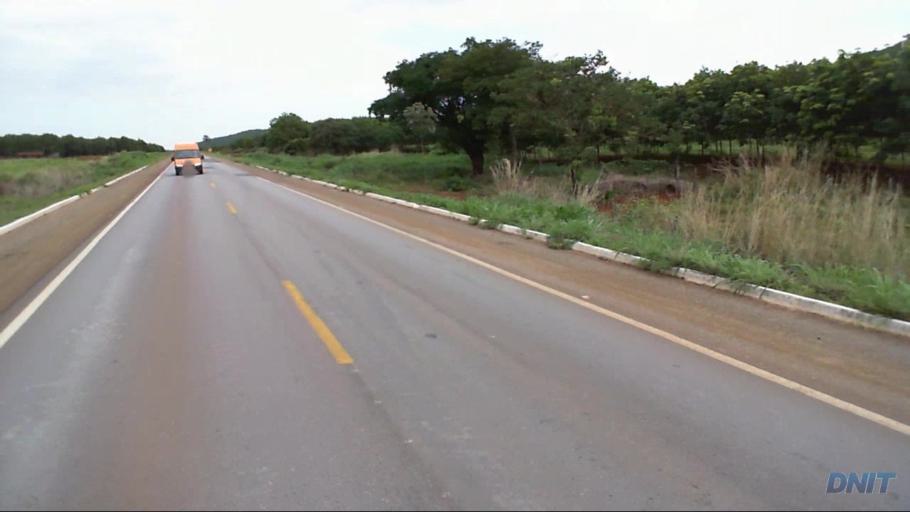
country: BR
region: Goias
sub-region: Barro Alto
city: Barro Alto
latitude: -14.9119
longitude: -48.9563
